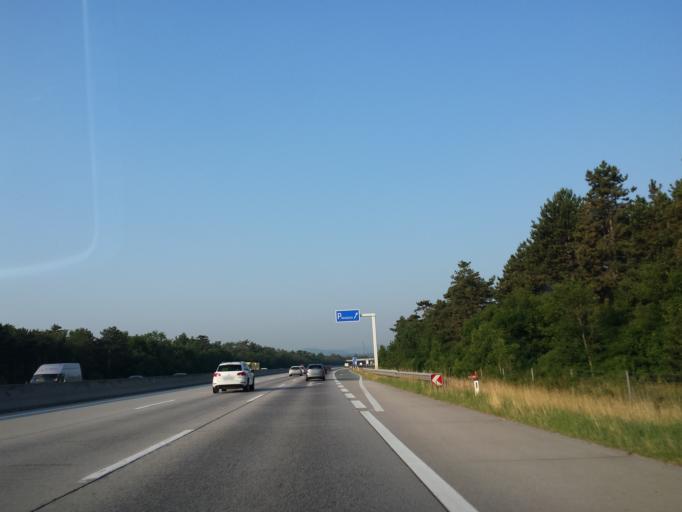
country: AT
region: Lower Austria
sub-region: Politischer Bezirk Wiener Neustadt
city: Bad Erlach
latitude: 47.7576
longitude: 16.1990
